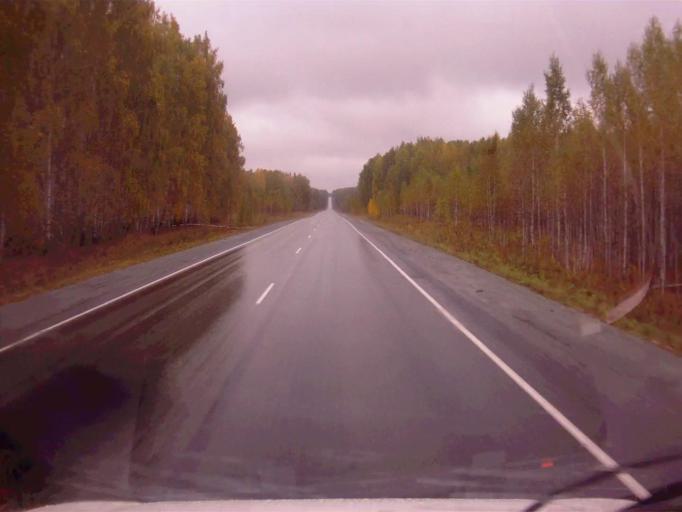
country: RU
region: Chelyabinsk
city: Tayginka
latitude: 55.5108
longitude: 60.6384
